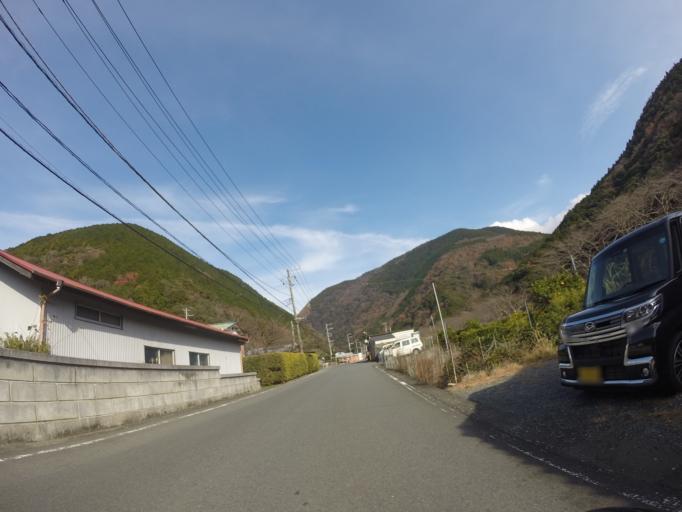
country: JP
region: Shizuoka
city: Heda
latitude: 34.7913
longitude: 138.8020
